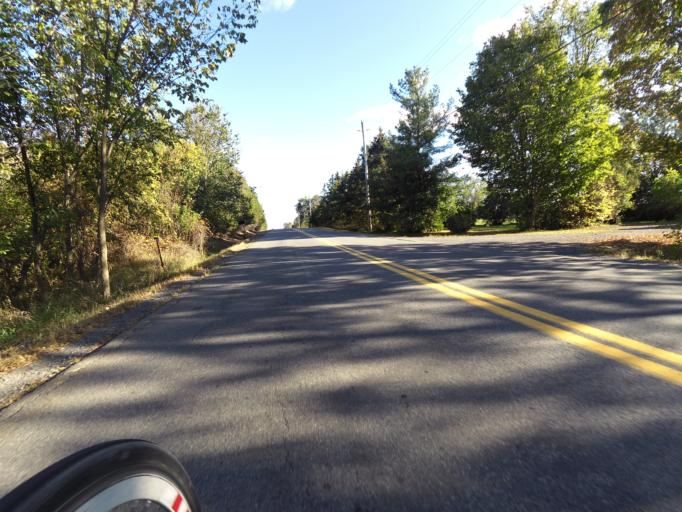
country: CA
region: Ontario
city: Bells Corners
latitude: 45.1674
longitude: -75.7936
